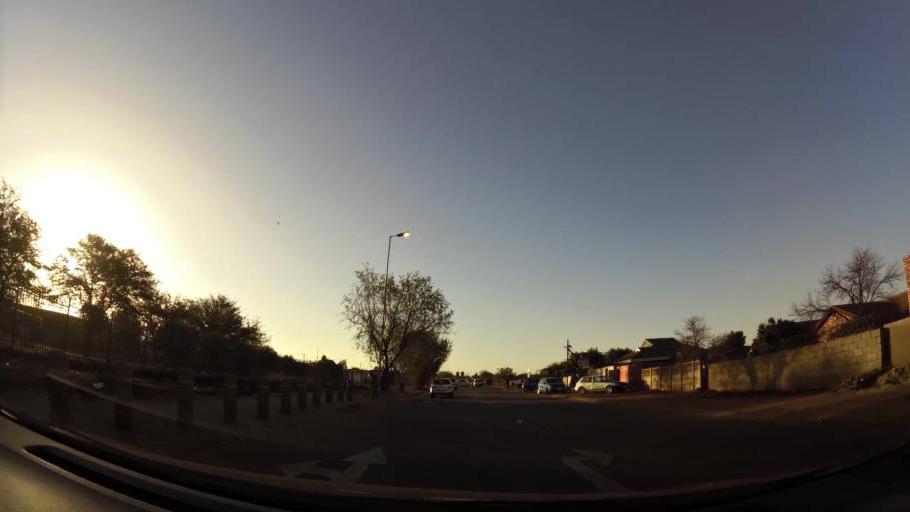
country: ZA
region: Gauteng
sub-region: City of Tshwane Metropolitan Municipality
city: Mabopane
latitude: -25.5894
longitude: 28.1074
